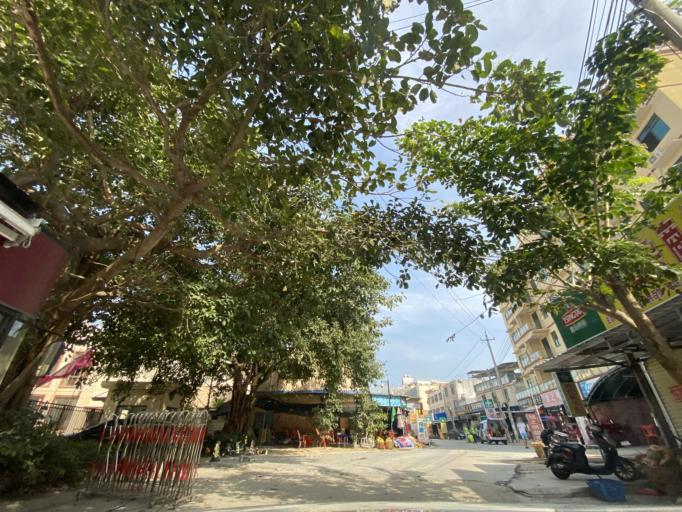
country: CN
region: Hainan
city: Yingzhou
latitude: 18.4041
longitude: 109.8419
